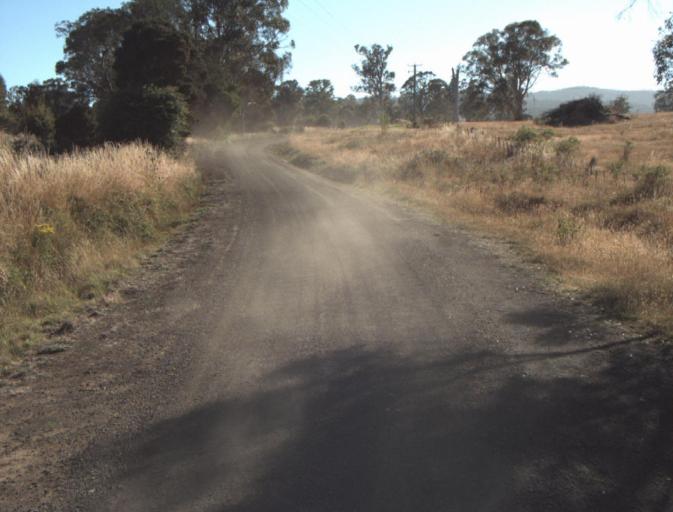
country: AU
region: Tasmania
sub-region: Launceston
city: Newstead
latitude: -41.4171
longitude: 147.2827
